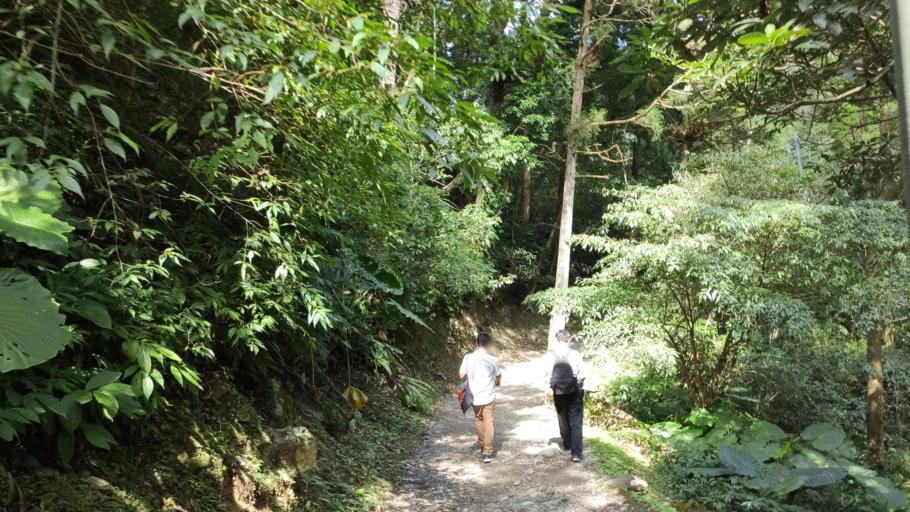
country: TW
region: Taiwan
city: Daxi
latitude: 24.8207
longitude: 121.4498
